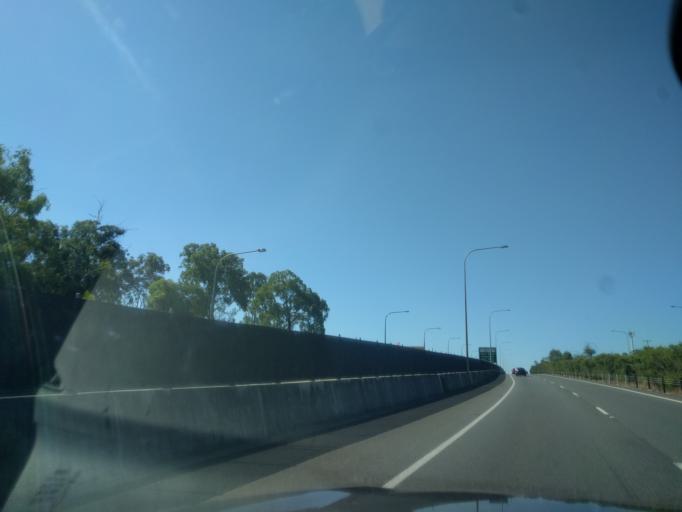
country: AU
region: Queensland
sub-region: Logan
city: Park Ridge South
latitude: -27.7090
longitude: 153.0379
